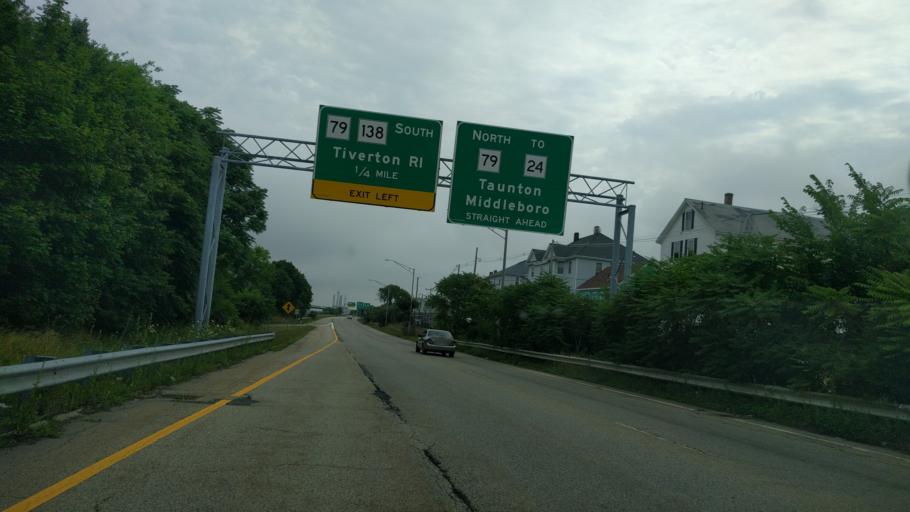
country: US
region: Massachusetts
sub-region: Bristol County
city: Fall River
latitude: 41.7186
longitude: -71.1536
